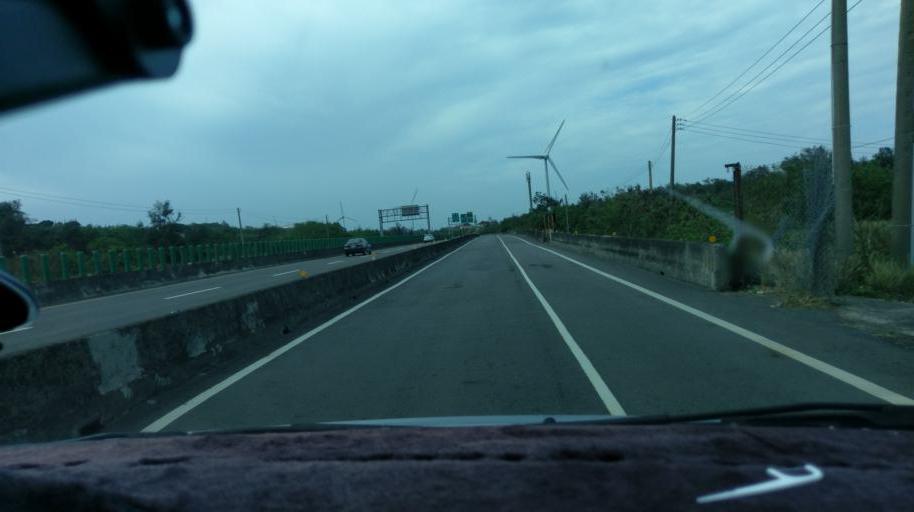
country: TW
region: Taiwan
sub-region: Hsinchu
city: Hsinchu
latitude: 24.7284
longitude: 120.8741
